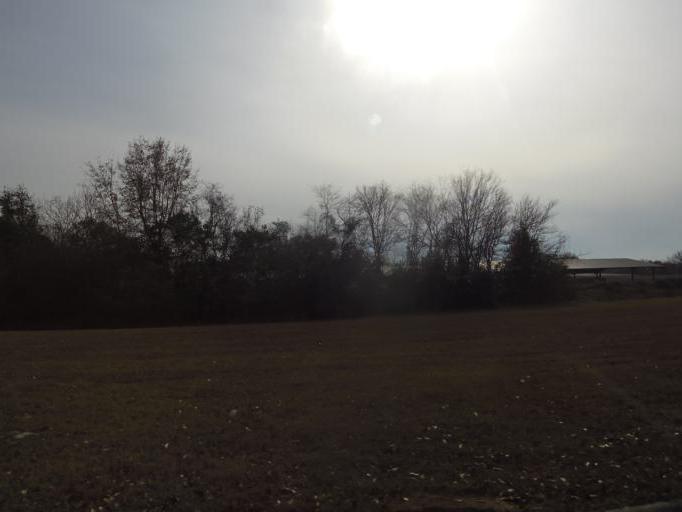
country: US
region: Alabama
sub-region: Houston County
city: Dothan
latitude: 31.2259
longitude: -85.3843
